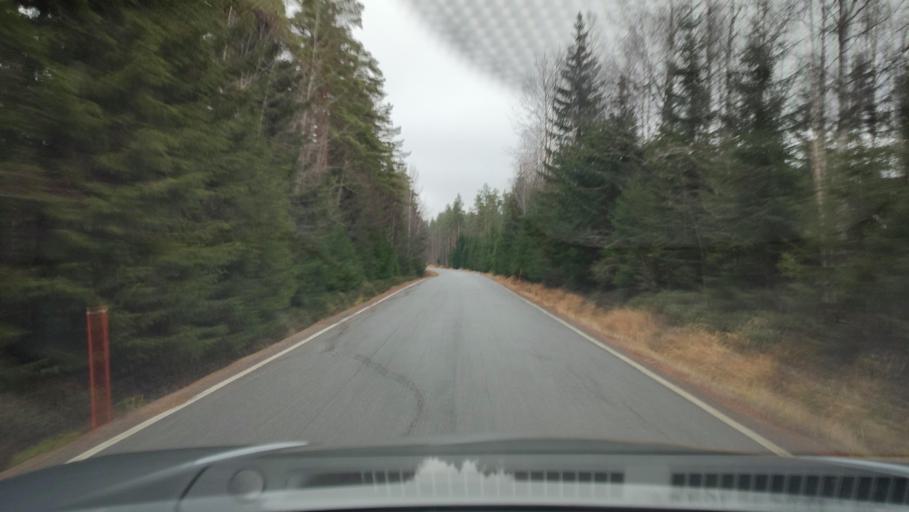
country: FI
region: Southern Ostrobothnia
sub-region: Suupohja
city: Isojoki
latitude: 62.1655
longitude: 21.8917
